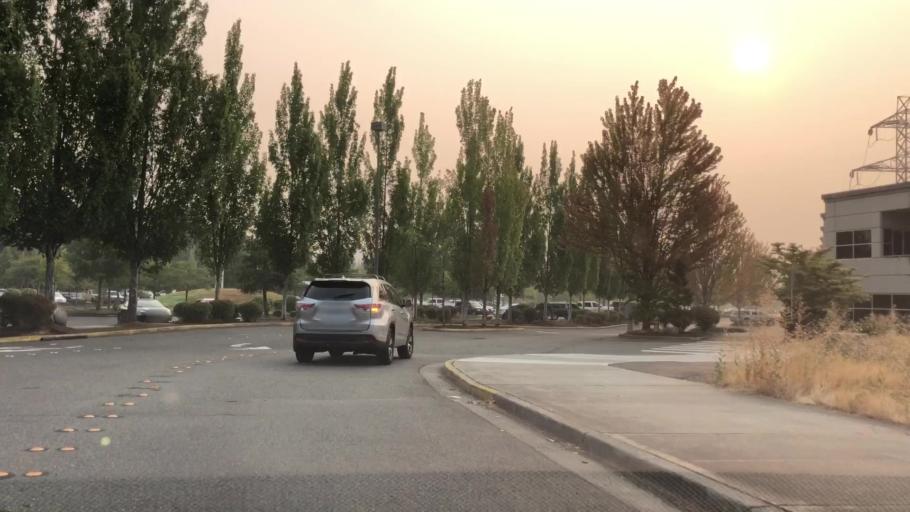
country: US
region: Washington
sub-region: King County
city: Redmond
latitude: 47.6885
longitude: -122.1485
